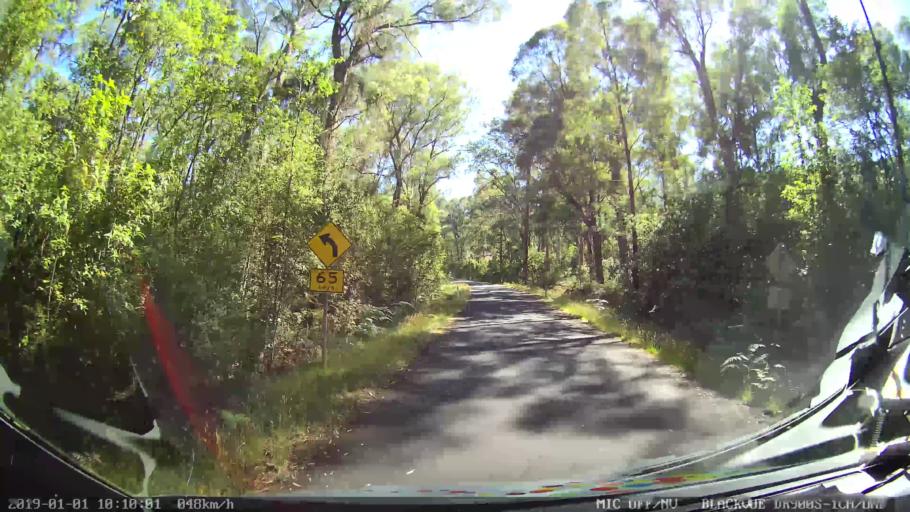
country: AU
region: New South Wales
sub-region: Snowy River
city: Jindabyne
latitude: -36.1441
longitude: 148.1577
